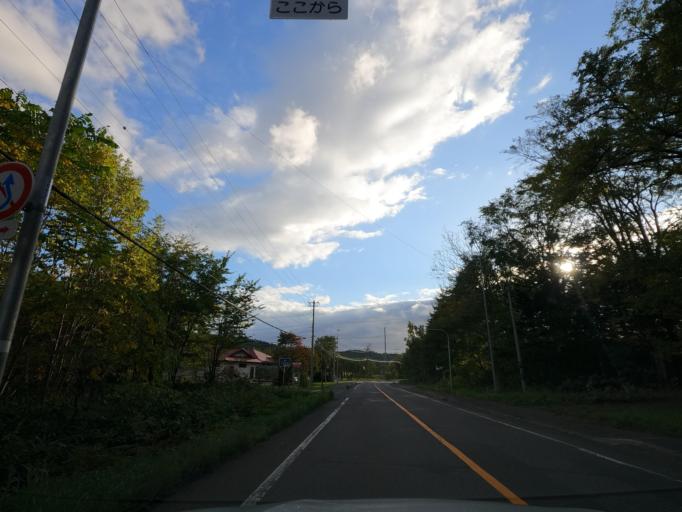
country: JP
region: Hokkaido
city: Date
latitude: 42.6422
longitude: 141.0501
